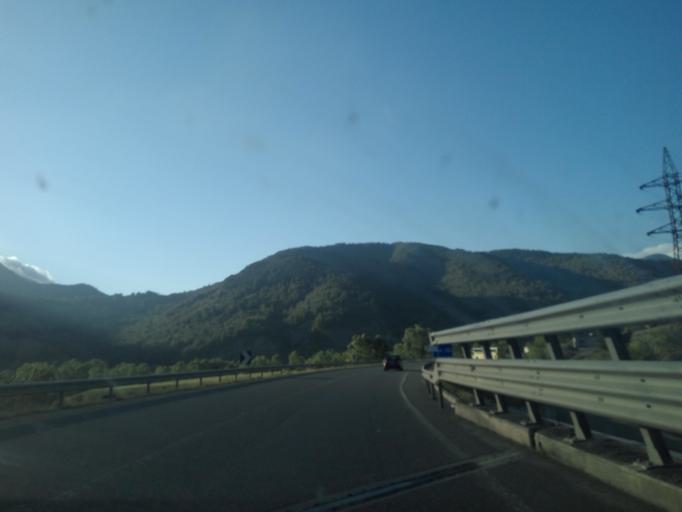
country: AL
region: Lezhe
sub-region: Rrethi i Mirdites
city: Rubik
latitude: 41.7801
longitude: 19.7839
